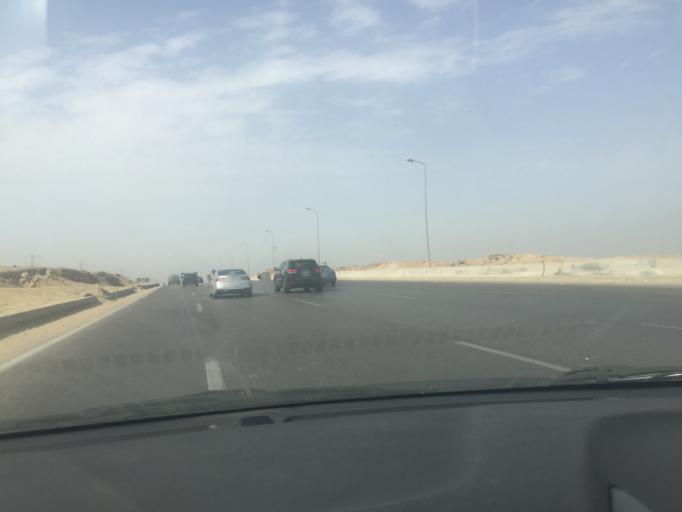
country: EG
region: Muhafazat al Qalyubiyah
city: Al Khankah
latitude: 30.0822
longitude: 31.4552
